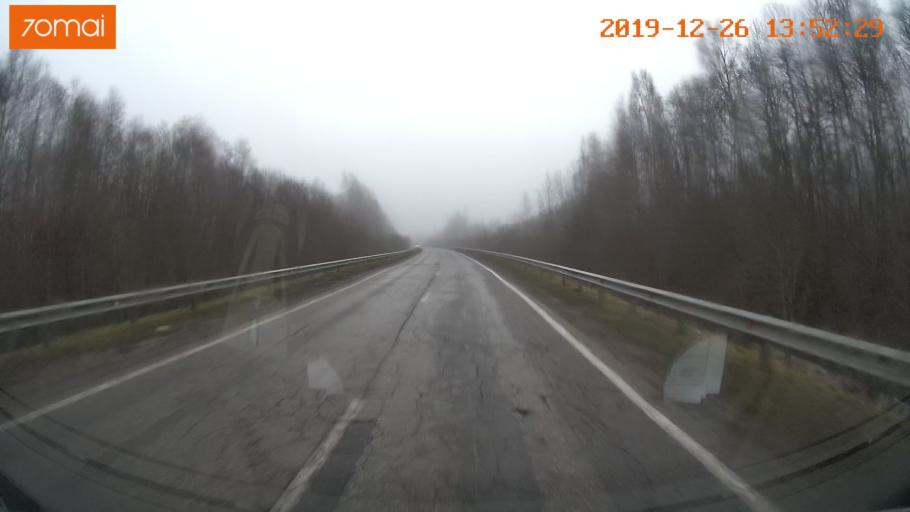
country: RU
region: Jaroslavl
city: Poshekhon'ye
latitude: 58.6312
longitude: 38.6021
